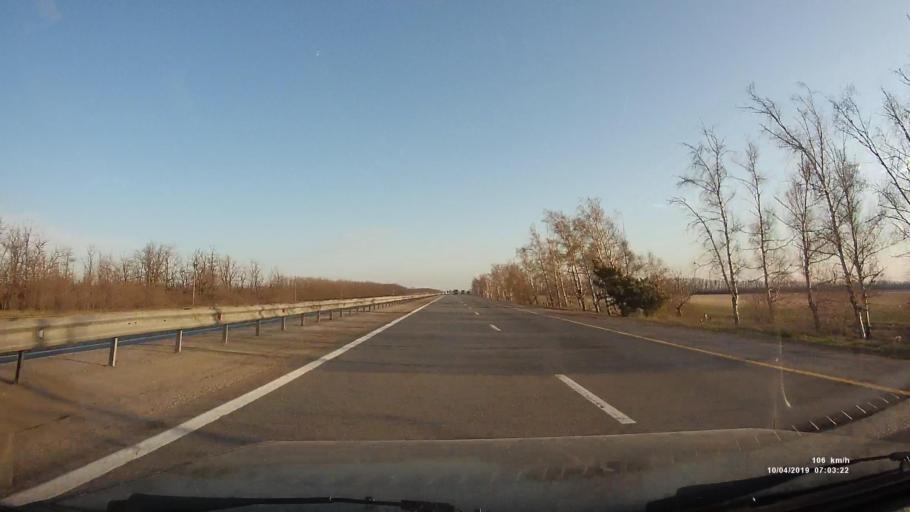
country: RU
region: Rostov
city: Mayskiy
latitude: 47.6217
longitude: 39.9947
